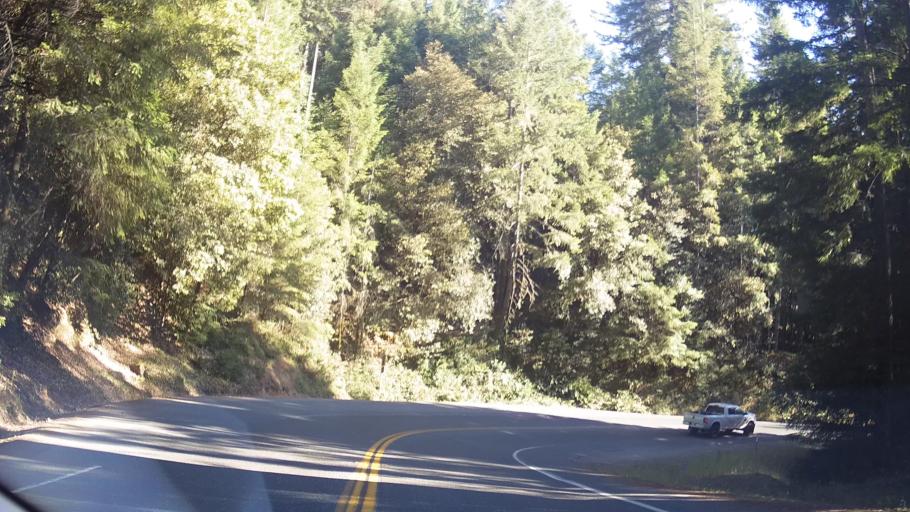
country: US
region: California
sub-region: Mendocino County
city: Brooktrails
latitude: 39.3617
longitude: -123.5056
